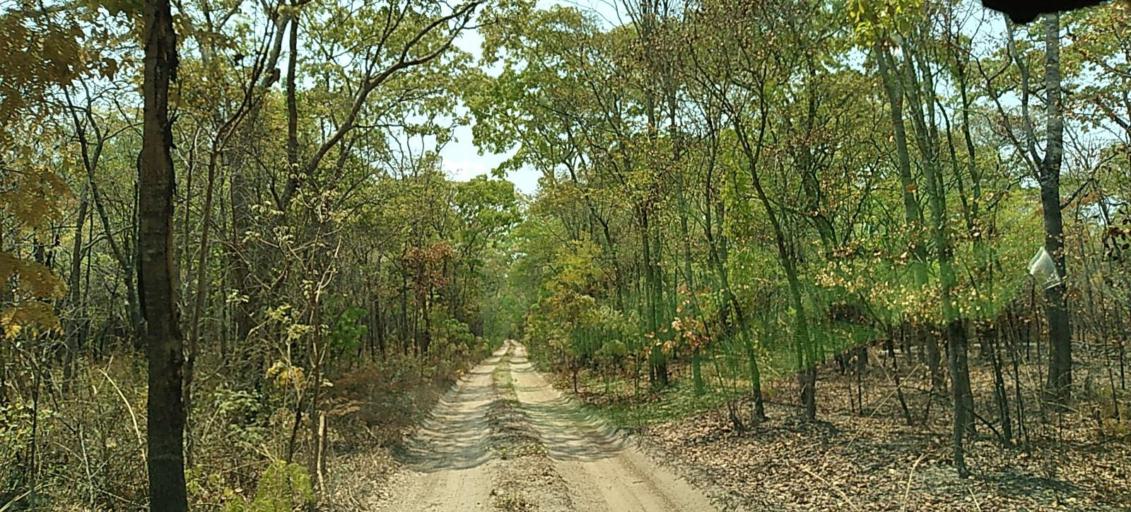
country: ZM
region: North-Western
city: Kabompo
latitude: -13.6489
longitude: 24.4765
